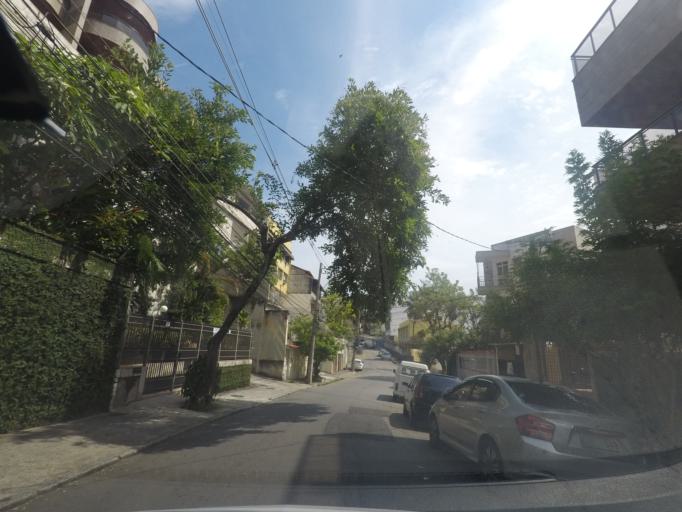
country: BR
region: Rio de Janeiro
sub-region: Rio De Janeiro
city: Rio de Janeiro
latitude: -22.8163
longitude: -43.1956
